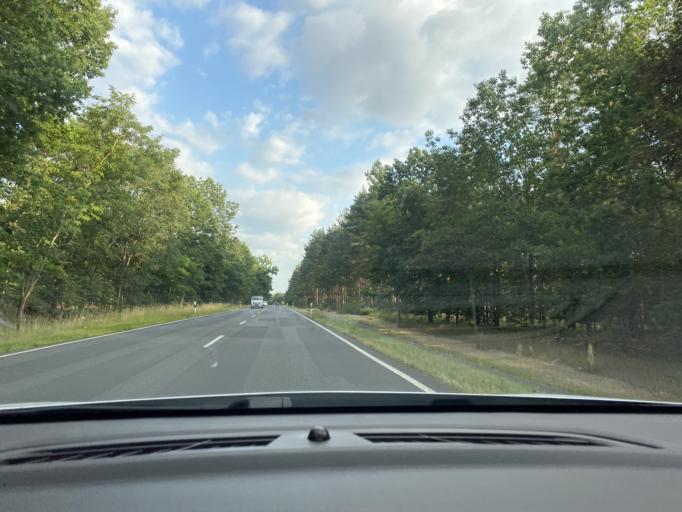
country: DE
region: Saxony
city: Konigswartha
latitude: 51.2969
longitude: 14.3268
